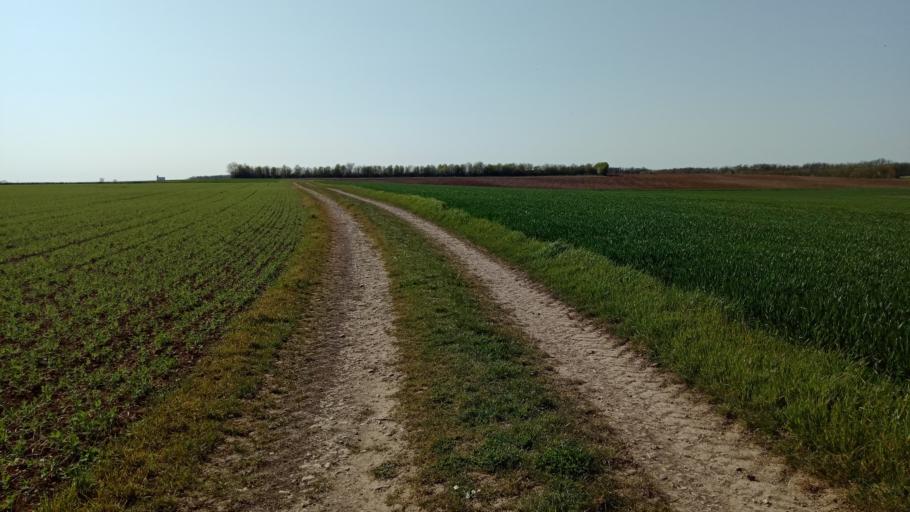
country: FR
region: Poitou-Charentes
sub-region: Departement de la Charente-Maritime
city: Verines
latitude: 46.1580
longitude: -0.9316
